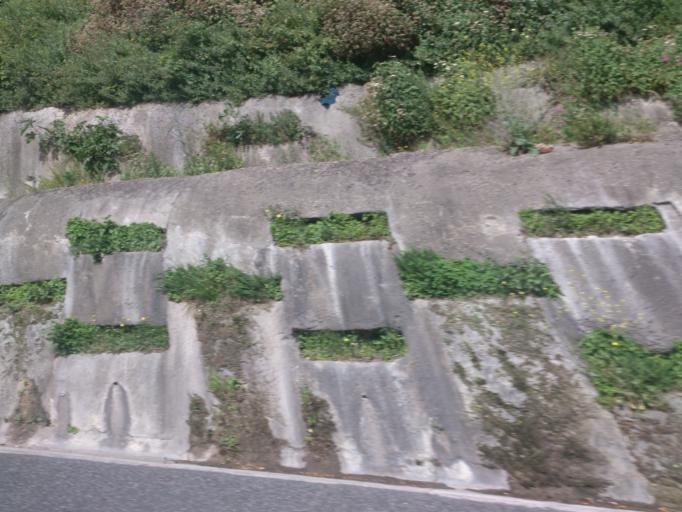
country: PT
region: Lisbon
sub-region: Loures
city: Sacavem
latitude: 38.7970
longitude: -9.1108
